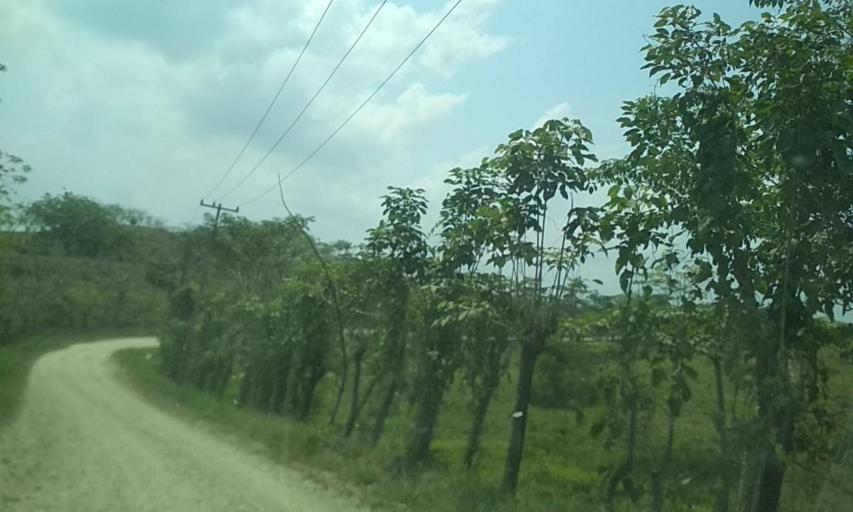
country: MX
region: Tabasco
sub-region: Huimanguillo
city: Francisco Rueda
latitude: 17.6312
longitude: -93.8218
